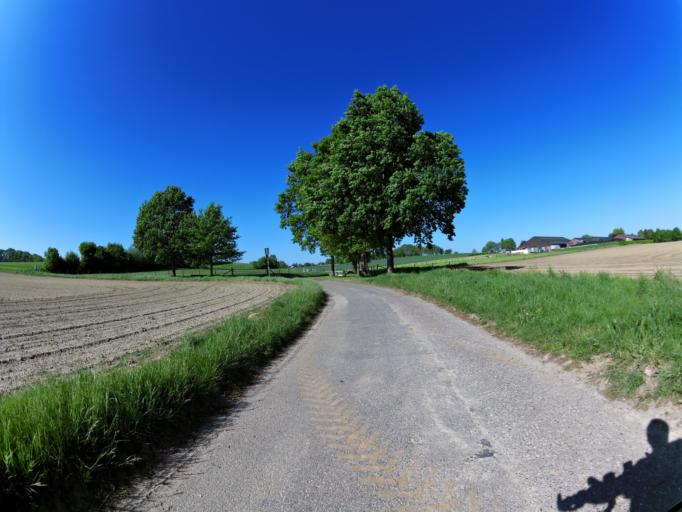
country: NL
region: Limburg
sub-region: Gemeente Onderbanken
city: Merkelbeek
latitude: 50.9640
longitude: 5.9418
